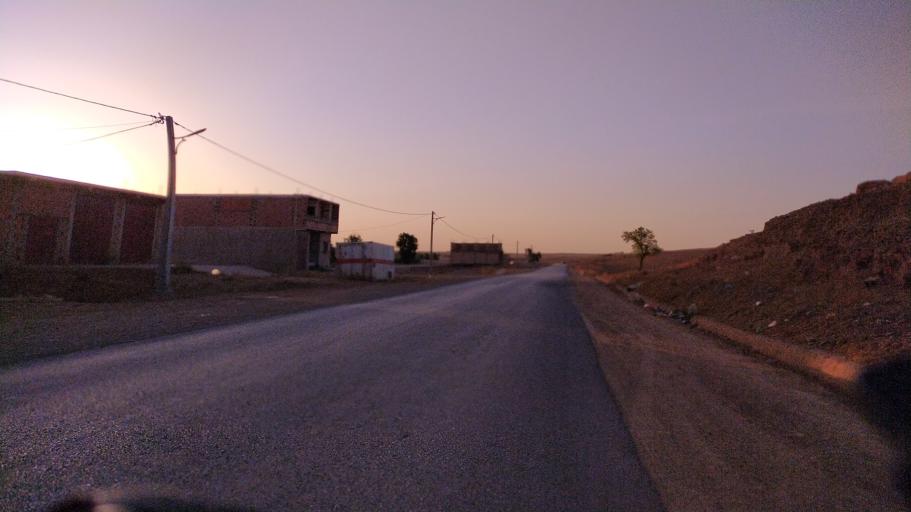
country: DZ
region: Tiaret
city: Frenda
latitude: 34.8993
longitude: 1.2455
